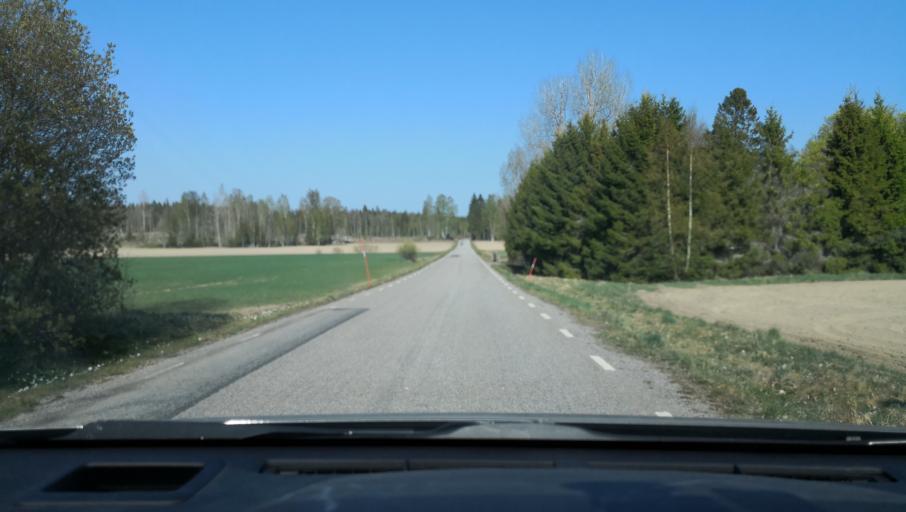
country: SE
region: Uppsala
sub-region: Heby Kommun
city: Heby
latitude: 60.0397
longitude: 16.8315
